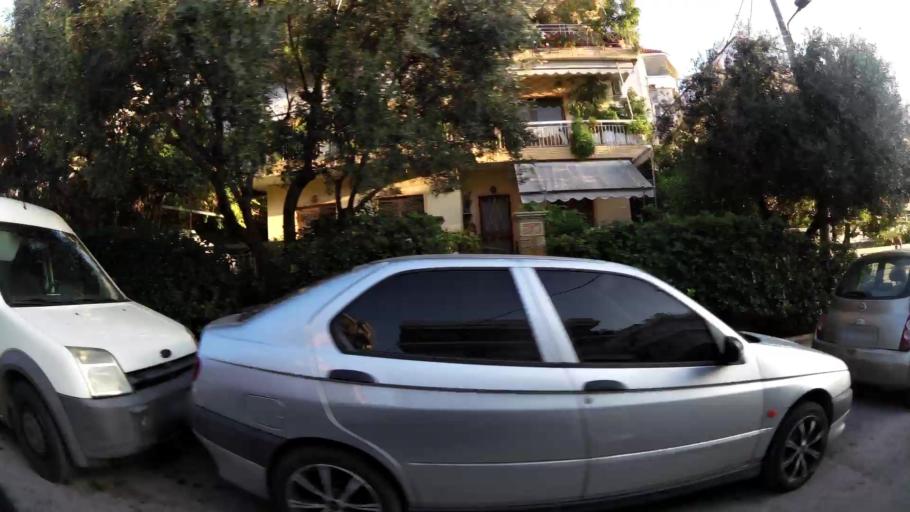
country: GR
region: Attica
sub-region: Nomarchia Athinas
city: Argyroupoli
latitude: 37.8916
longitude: 23.7678
